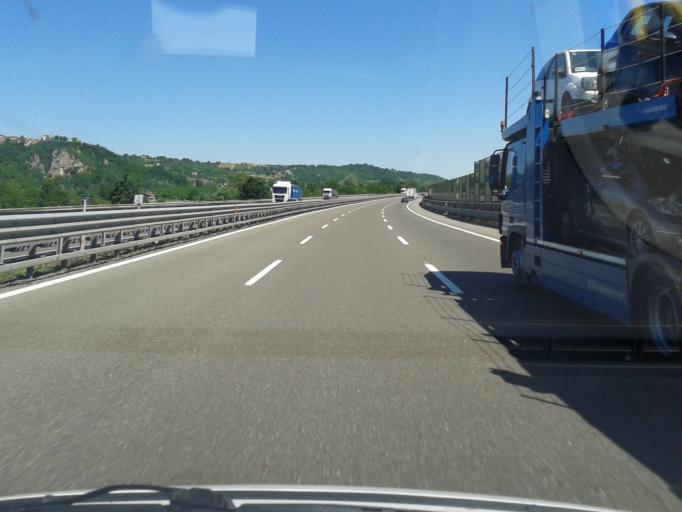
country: IT
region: Piedmont
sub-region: Provincia di Alessandria
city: Rocca Grimalda
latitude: 44.6599
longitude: 8.6590
